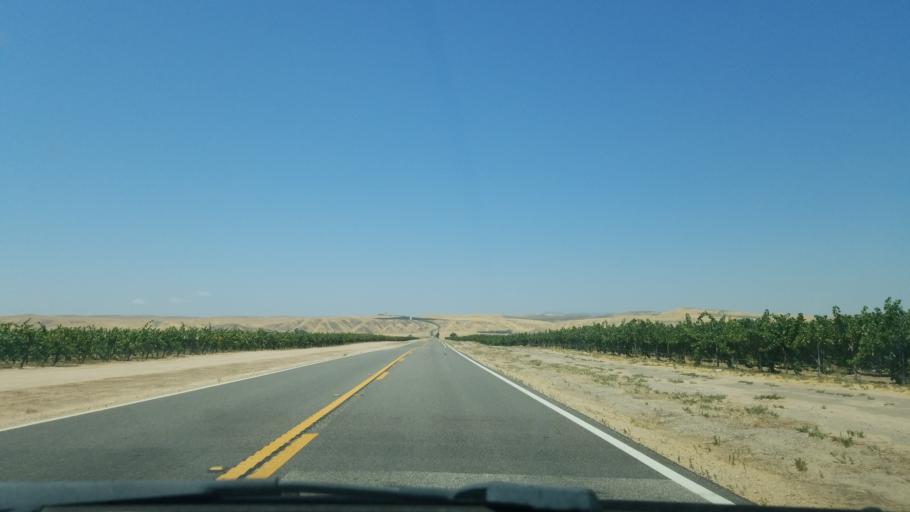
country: US
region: California
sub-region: San Luis Obispo County
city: Shandon
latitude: 35.6316
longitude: -120.3998
